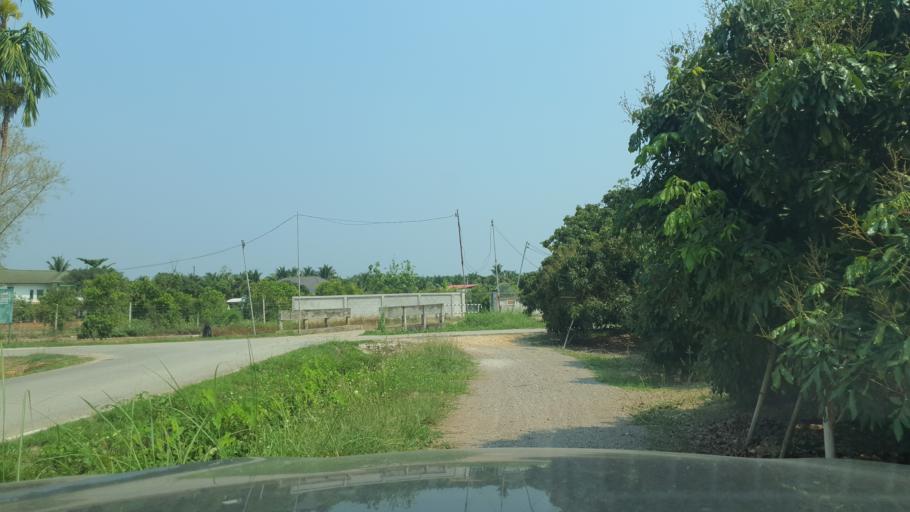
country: TH
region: Chiang Mai
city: Saraphi
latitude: 18.6707
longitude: 98.9975
